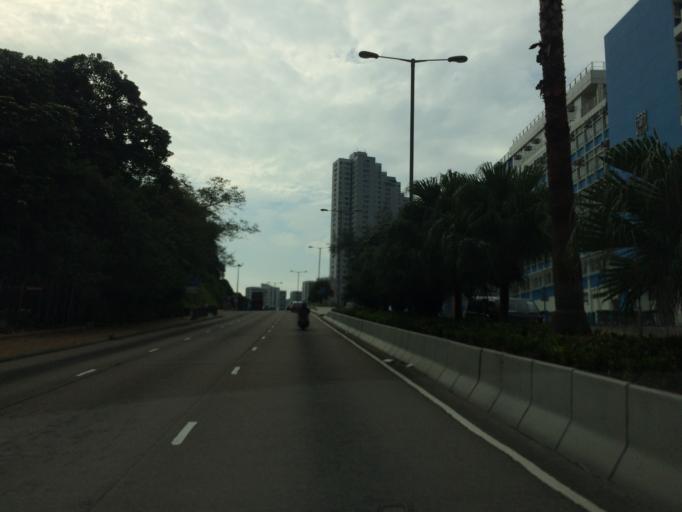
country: HK
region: Wanchai
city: Wan Chai
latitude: 22.2723
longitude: 114.2329
